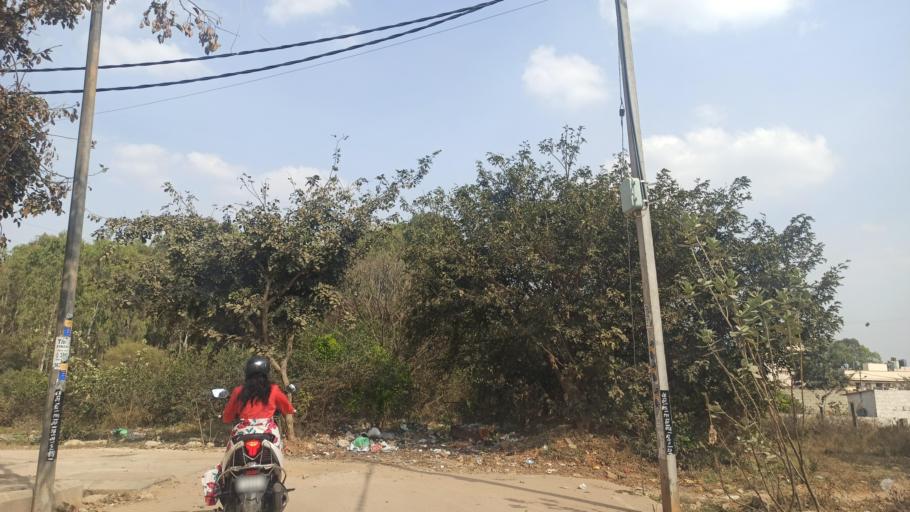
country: IN
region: Karnataka
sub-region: Bangalore Urban
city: Yelahanka
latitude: 13.1128
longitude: 77.6098
